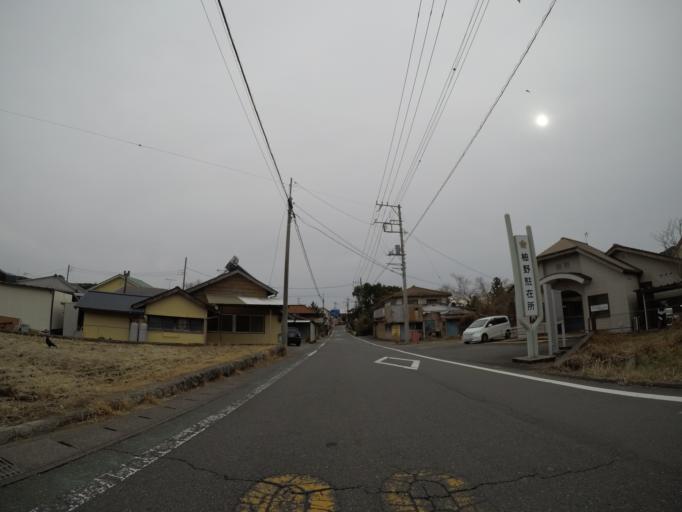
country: JP
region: Shizuoka
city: Fujinomiya
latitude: 35.2567
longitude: 138.5554
